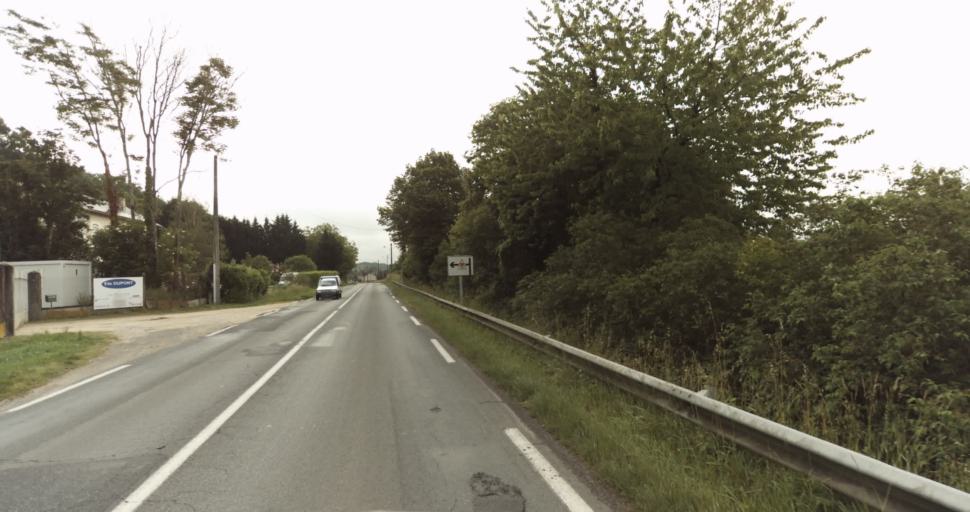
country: FR
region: Aquitaine
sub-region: Departement de la Dordogne
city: Creysse
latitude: 44.8551
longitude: 0.5810
